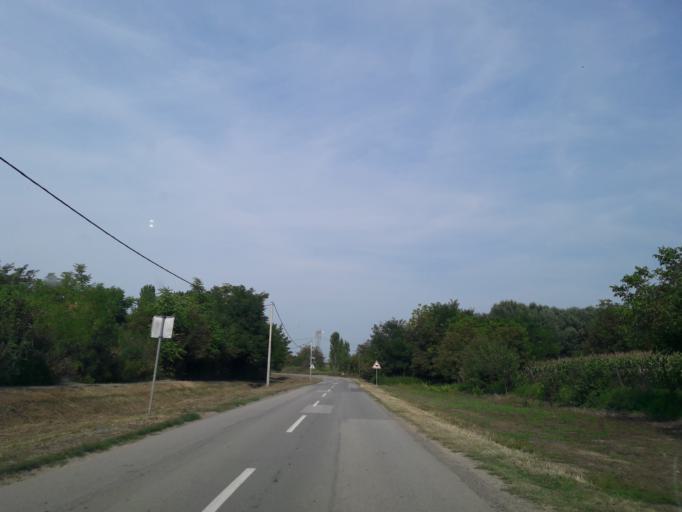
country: HR
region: Vukovarsko-Srijemska
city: Bobota
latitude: 45.3766
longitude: 18.8518
